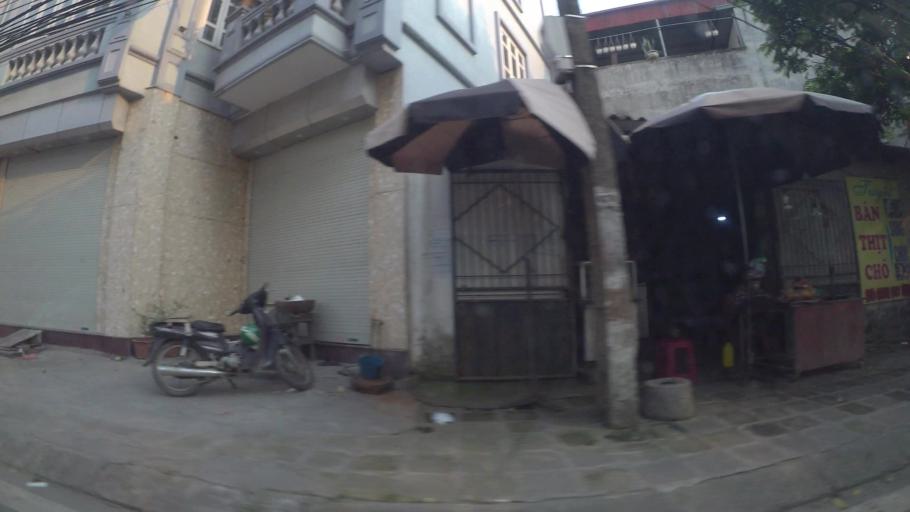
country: VN
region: Ha Noi
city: Van Dien
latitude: 20.9241
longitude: 105.8492
